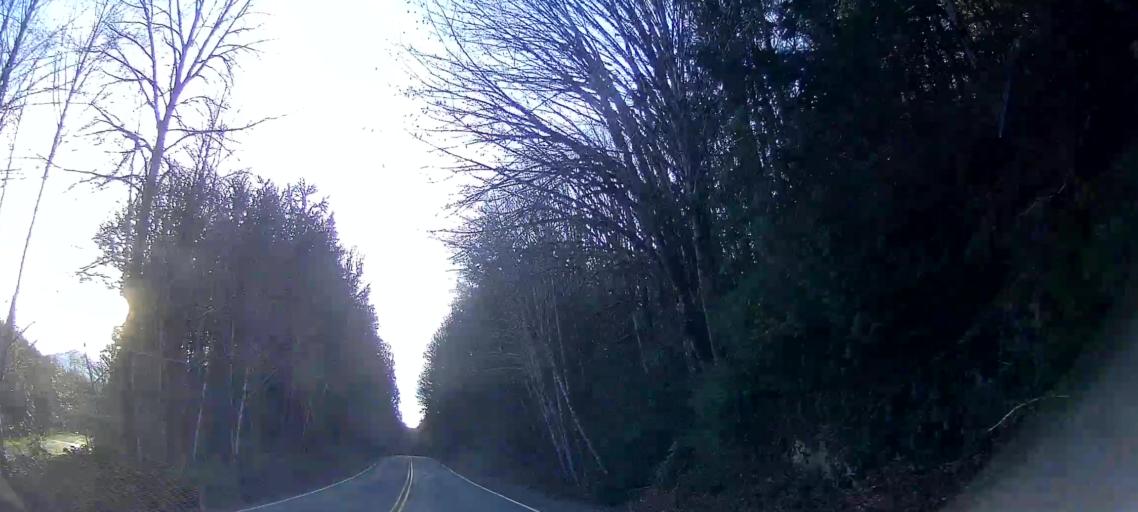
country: US
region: Washington
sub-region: Snohomish County
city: Darrington
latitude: 48.5674
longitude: -121.8035
